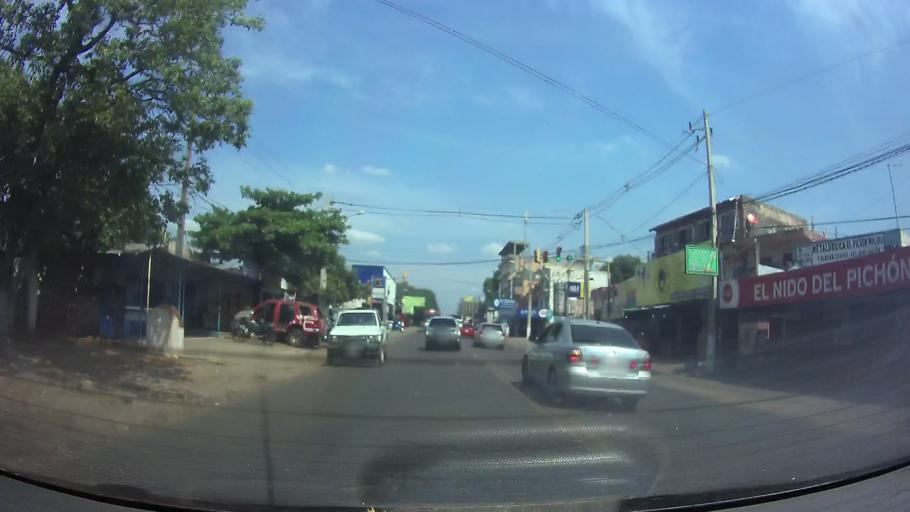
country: PY
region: Central
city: San Lorenzo
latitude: -25.3627
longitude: -57.4836
